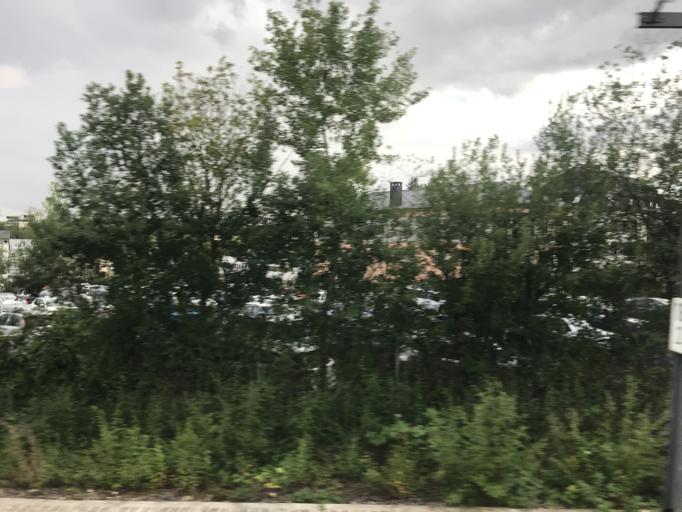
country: LU
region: Luxembourg
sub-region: Canton de Luxembourg
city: Luxembourg
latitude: 49.5965
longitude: 6.1103
